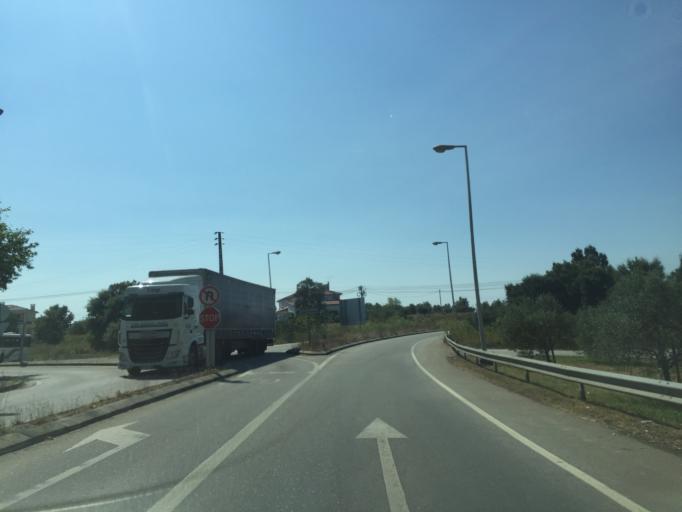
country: PT
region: Aveiro
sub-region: Mealhada
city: Mealhada
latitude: 40.3668
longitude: -8.4561
